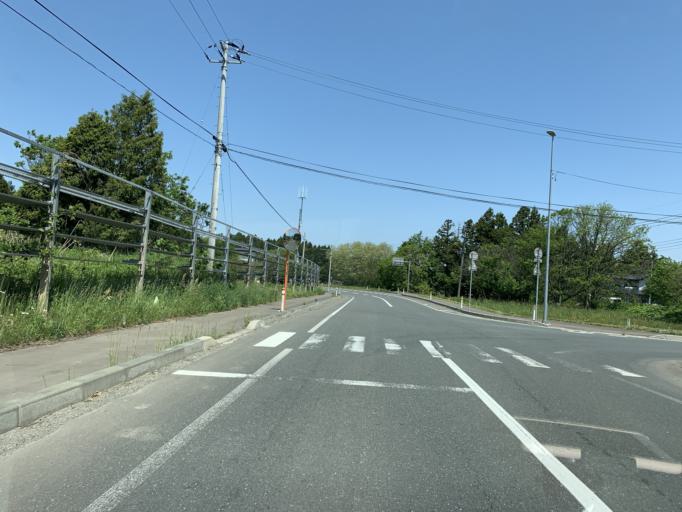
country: JP
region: Iwate
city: Kitakami
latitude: 39.2614
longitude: 141.0634
